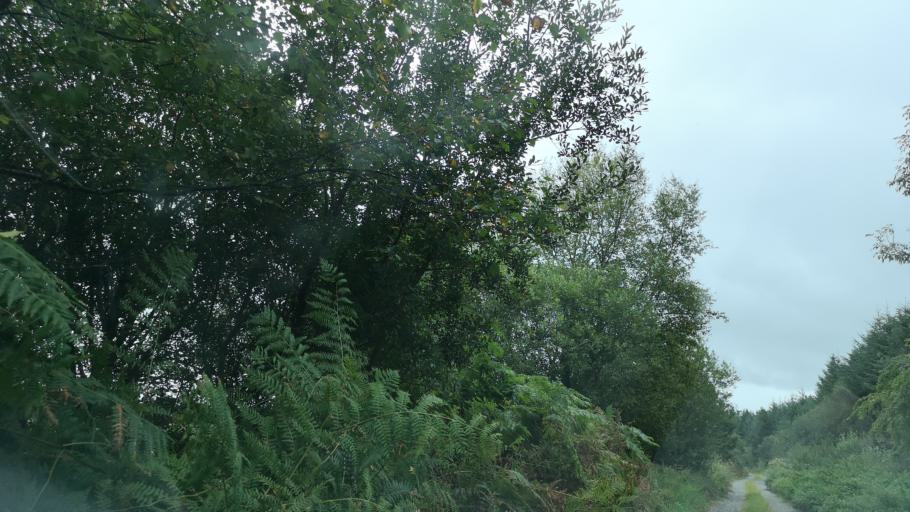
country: IE
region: Connaught
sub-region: County Galway
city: Athenry
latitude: 53.3039
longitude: -8.6603
